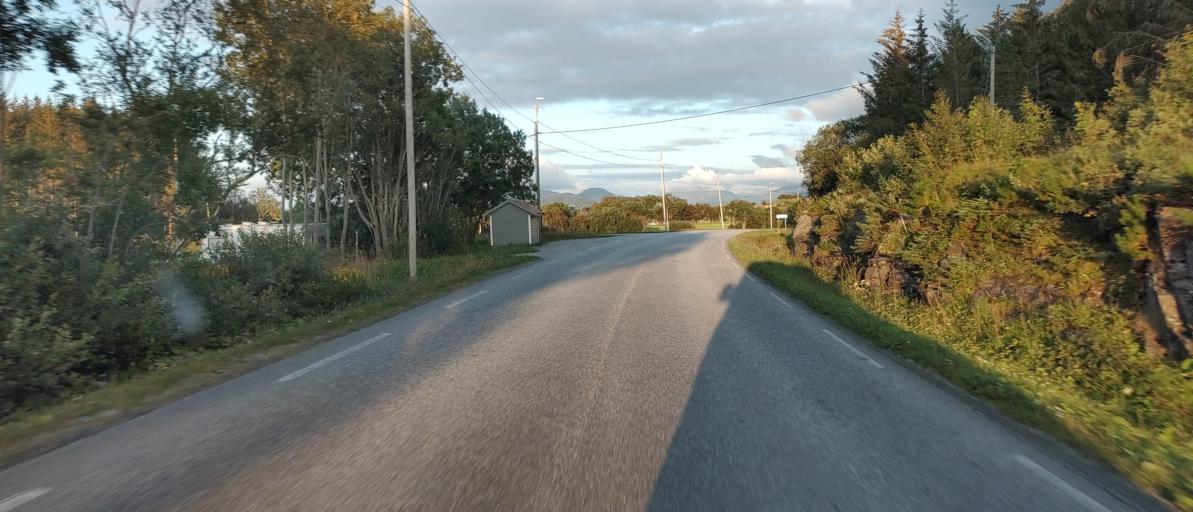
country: NO
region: More og Romsdal
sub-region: Fraena
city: Elnesvagen
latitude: 62.9914
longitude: 7.1946
